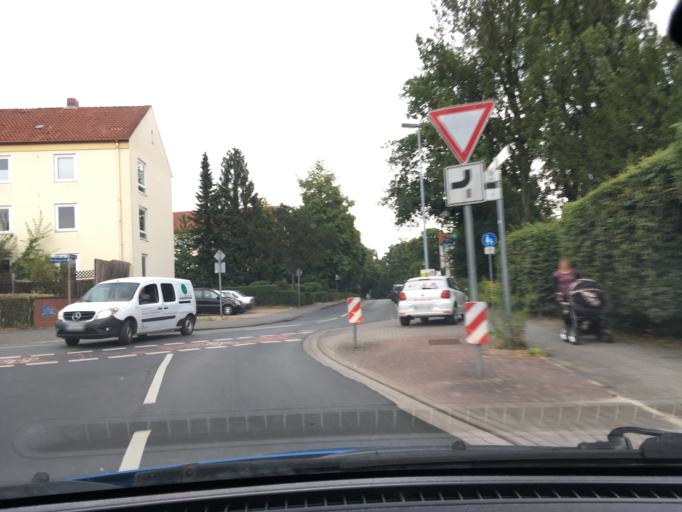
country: DE
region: Lower Saxony
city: Celle
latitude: 52.6270
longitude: 10.0999
